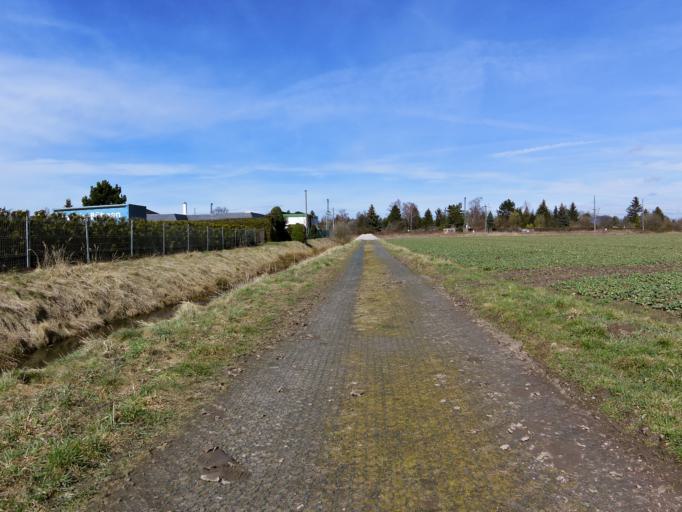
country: DE
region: Saxony
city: Borsdorf
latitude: 51.3422
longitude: 12.4923
